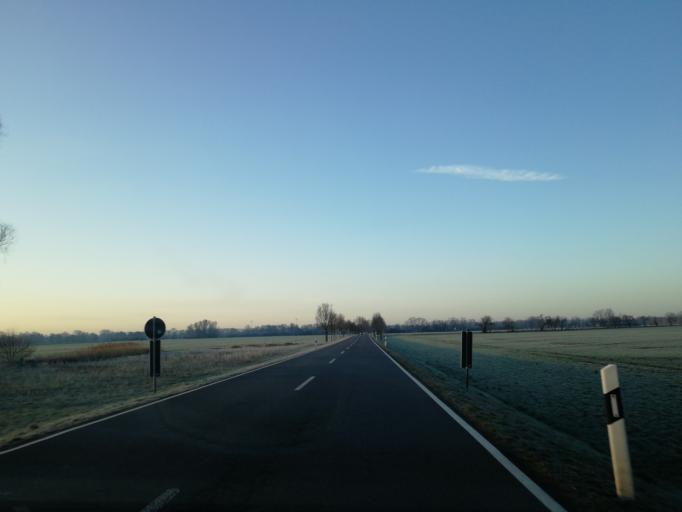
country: DE
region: Brandenburg
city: Finsterwalde
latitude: 51.6822
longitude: 13.7219
